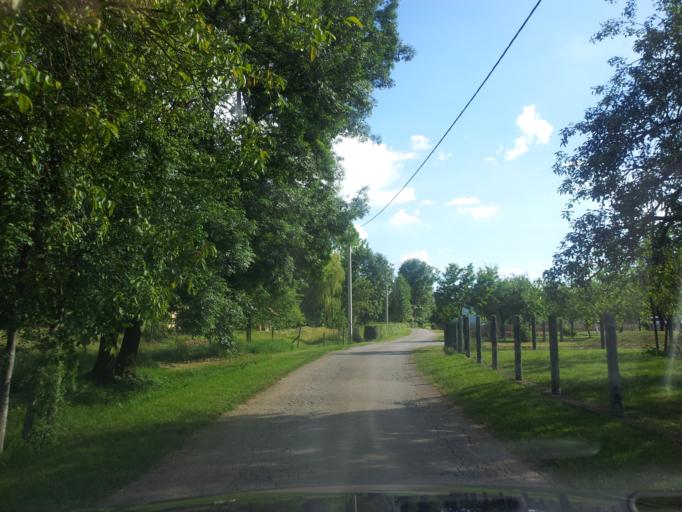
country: HR
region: Karlovacka
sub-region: Grad Karlovac
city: Karlovac
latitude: 45.4326
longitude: 15.4990
